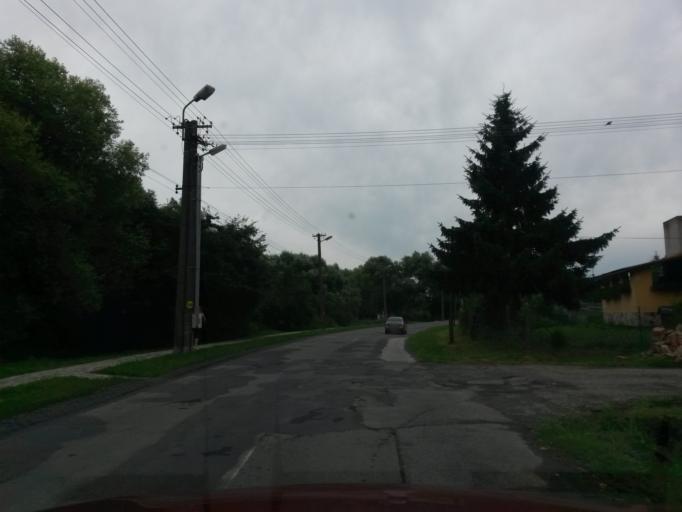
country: SK
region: Nitriansky
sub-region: Okres Nitra
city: Vrable
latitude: 48.1397
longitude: 18.4014
